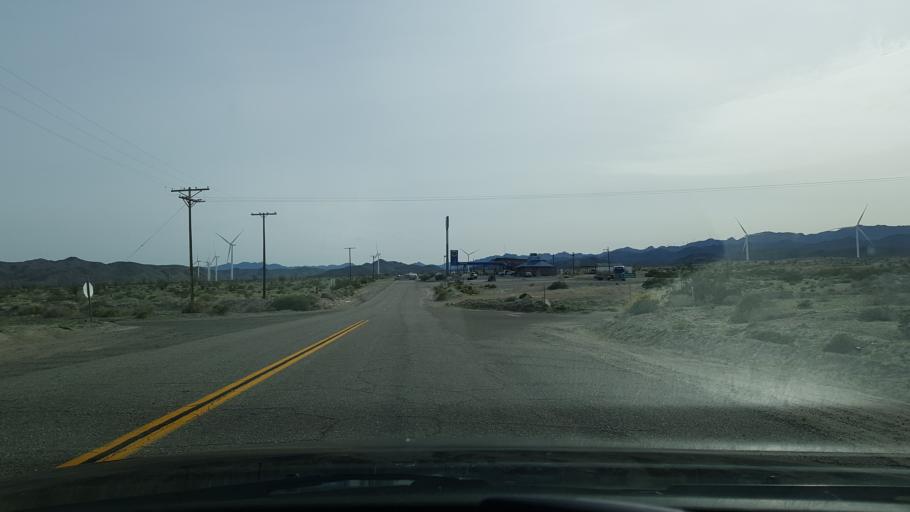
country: US
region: California
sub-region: Imperial County
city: Seeley
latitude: 32.7331
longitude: -115.9942
